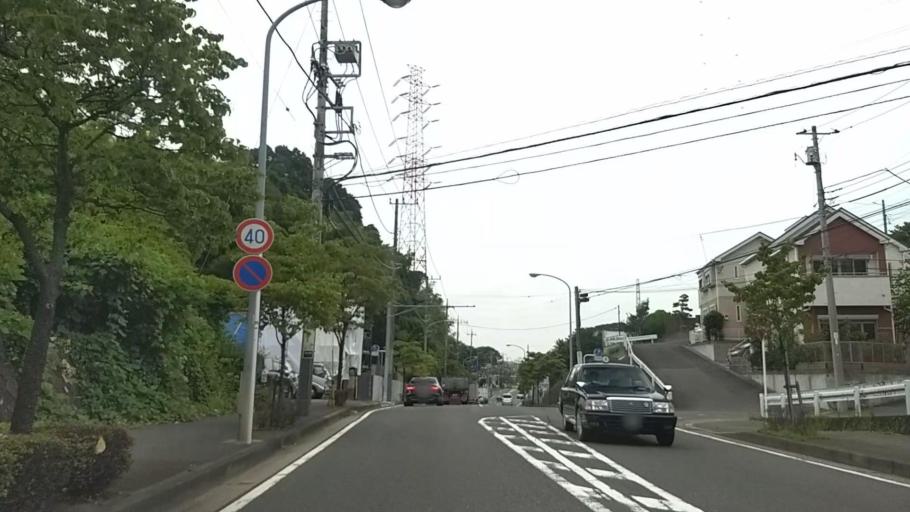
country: JP
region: Kanagawa
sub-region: Kawasaki-shi
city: Kawasaki
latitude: 35.5599
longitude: 139.6088
